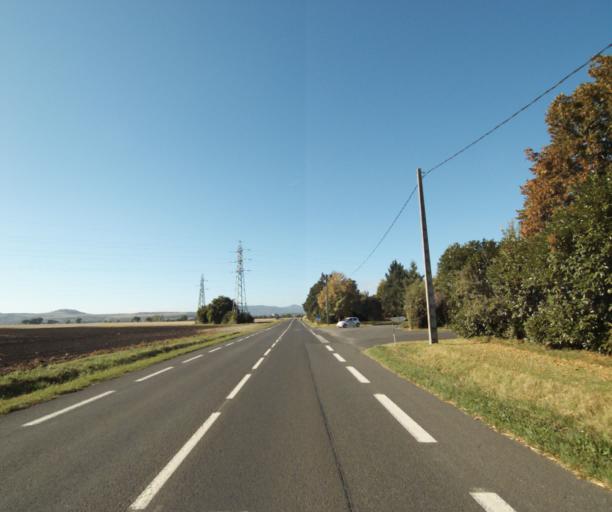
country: FR
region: Auvergne
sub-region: Departement du Puy-de-Dome
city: Malintrat
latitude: 45.8074
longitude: 3.1884
